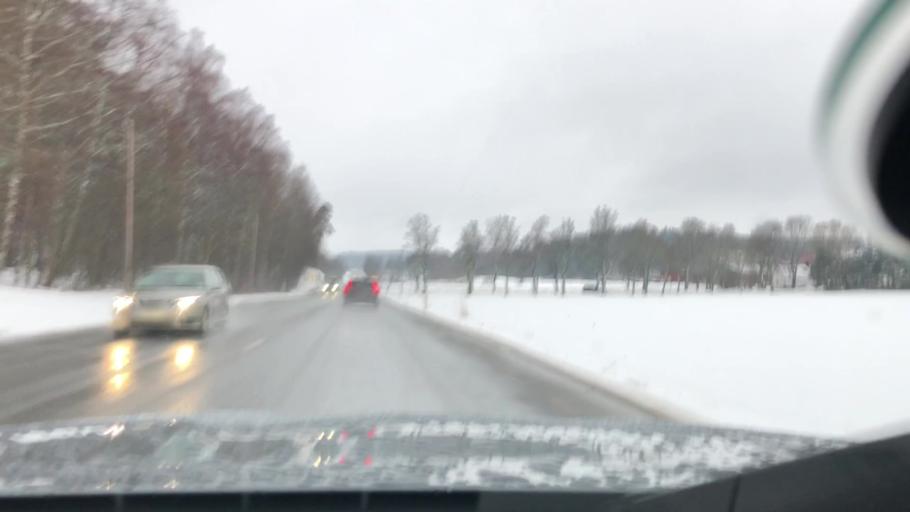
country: SE
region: Stockholm
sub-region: Sodertalje Kommun
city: Pershagen
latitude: 59.0566
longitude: 17.6125
